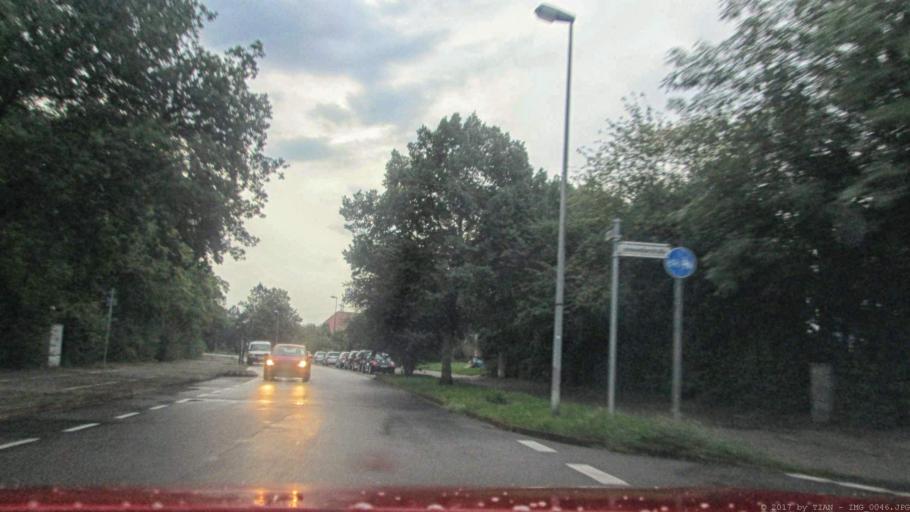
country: DE
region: Lower Saxony
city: Weyhausen
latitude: 52.4105
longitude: 10.7250
